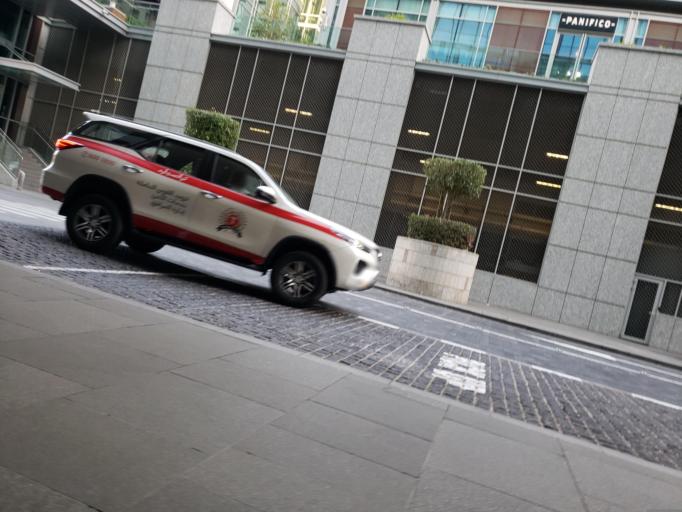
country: AE
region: Ash Shariqah
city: Sharjah
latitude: 25.2144
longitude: 55.2824
